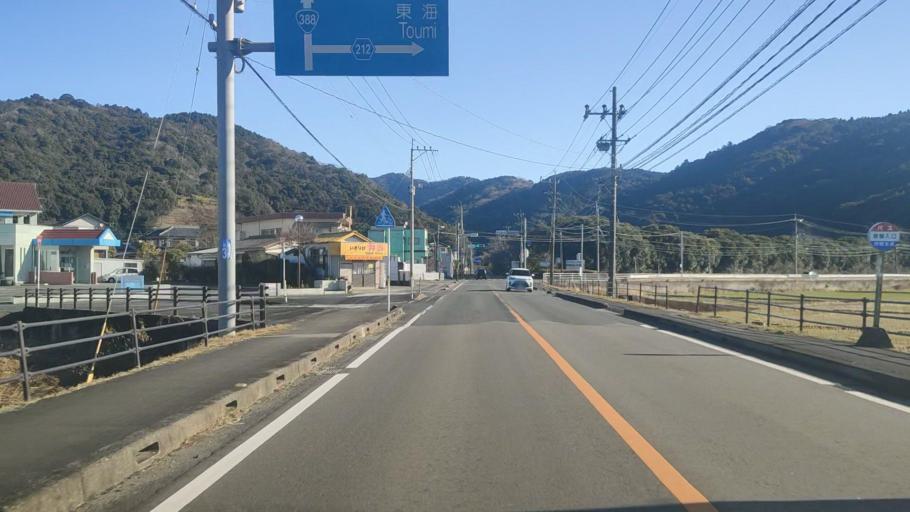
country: JP
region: Miyazaki
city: Nobeoka
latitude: 32.6174
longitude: 131.6990
